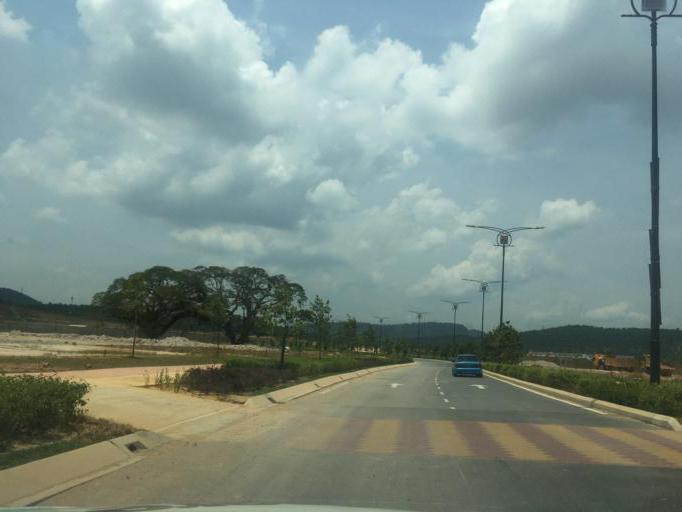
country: MY
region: Putrajaya
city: Putrajaya
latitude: 2.8453
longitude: 101.7037
